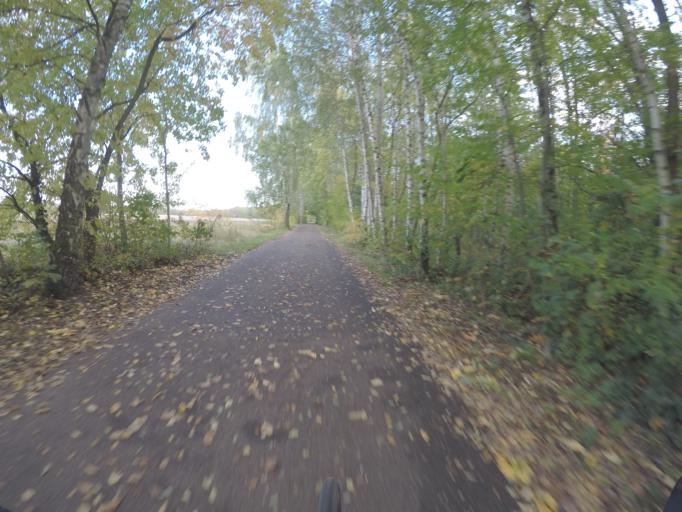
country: DE
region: Berlin
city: Frohnau
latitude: 52.6405
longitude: 13.2663
